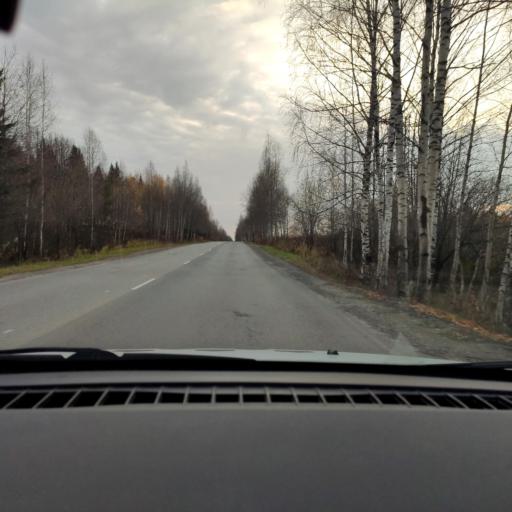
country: RU
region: Perm
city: Polazna
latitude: 58.1043
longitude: 56.4157
